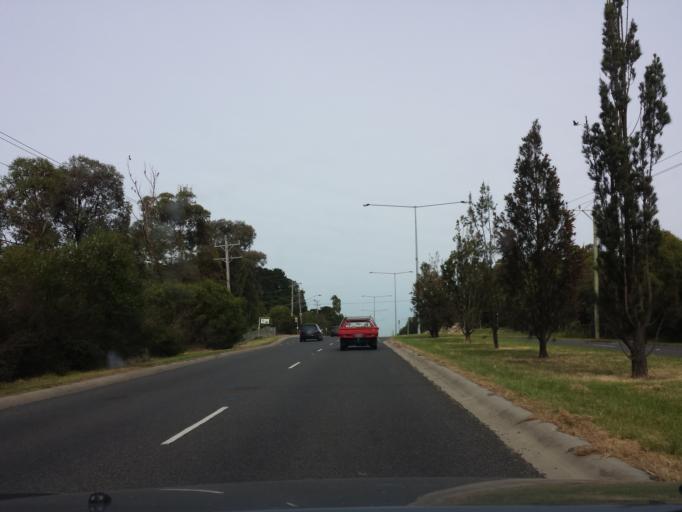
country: AU
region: Victoria
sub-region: Knox
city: Wantirna South
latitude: -37.8769
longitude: 145.2014
